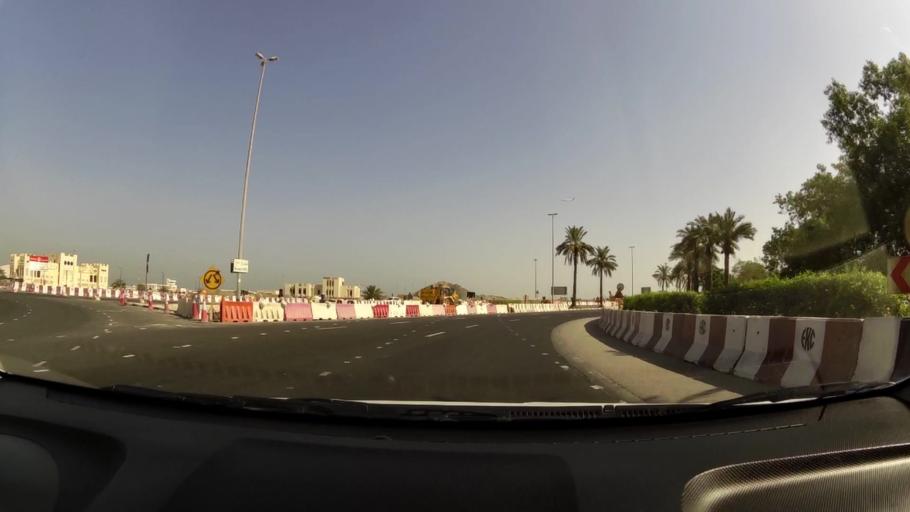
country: AE
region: Ash Shariqah
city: Sharjah
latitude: 25.2743
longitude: 55.2972
